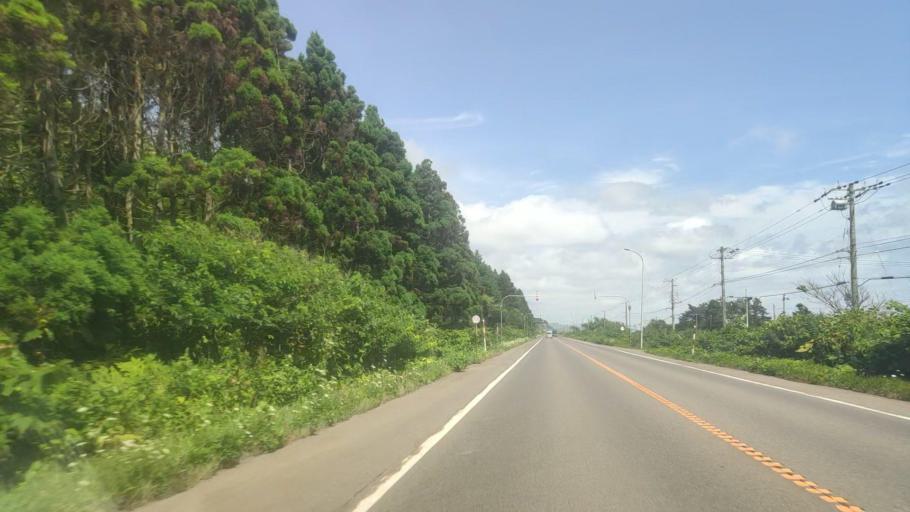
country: JP
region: Hokkaido
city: Niseko Town
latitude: 42.3406
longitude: 140.2807
